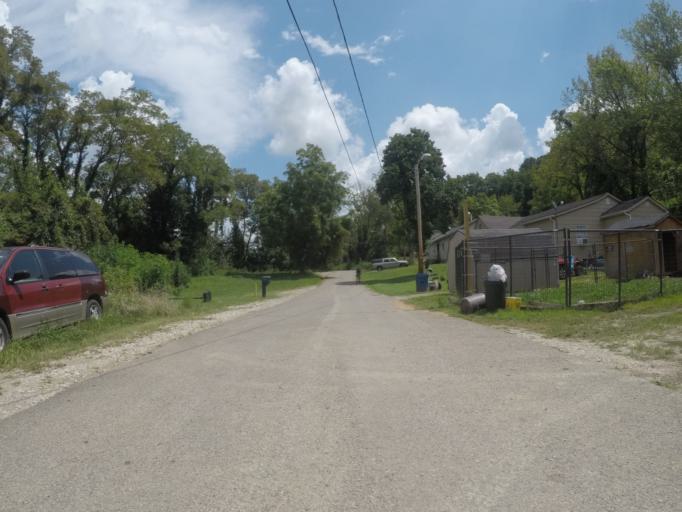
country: US
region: West Virginia
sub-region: Cabell County
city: Pea Ridge
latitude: 38.4272
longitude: -82.3764
